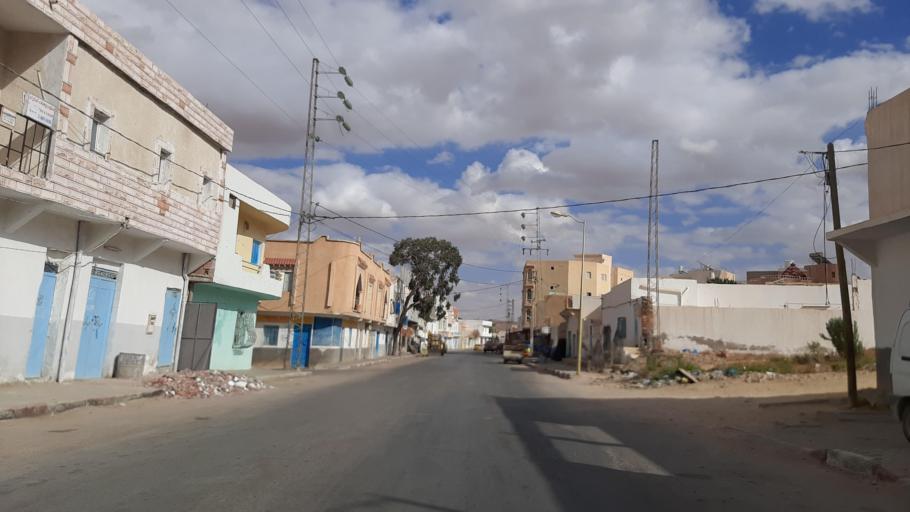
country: TN
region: Tataouine
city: Tataouine
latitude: 32.9257
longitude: 10.4531
